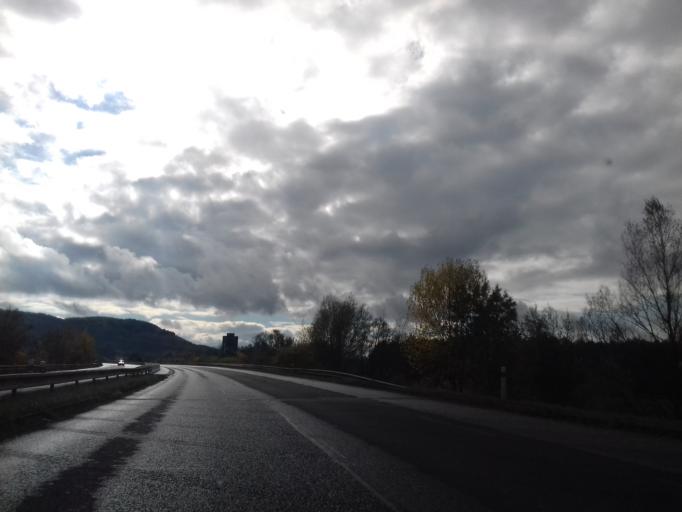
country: CZ
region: Central Bohemia
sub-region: Okres Mlada Boleslav
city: Zd'ar
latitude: 50.5536
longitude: 15.0446
